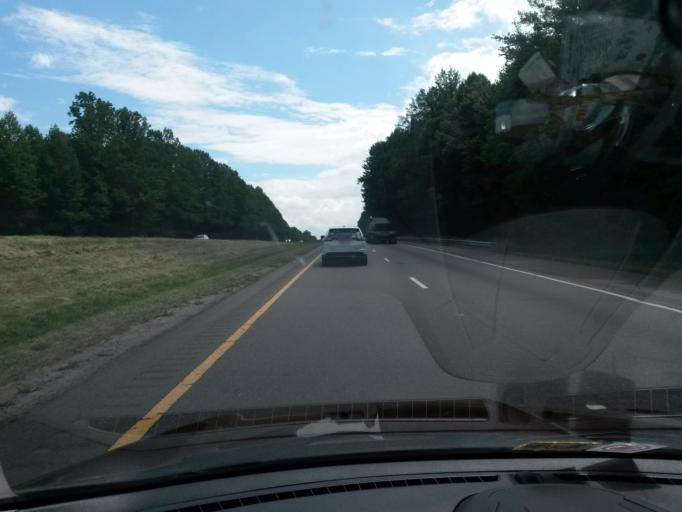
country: US
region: North Carolina
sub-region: Surry County
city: Dobson
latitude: 36.4237
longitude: -80.7767
